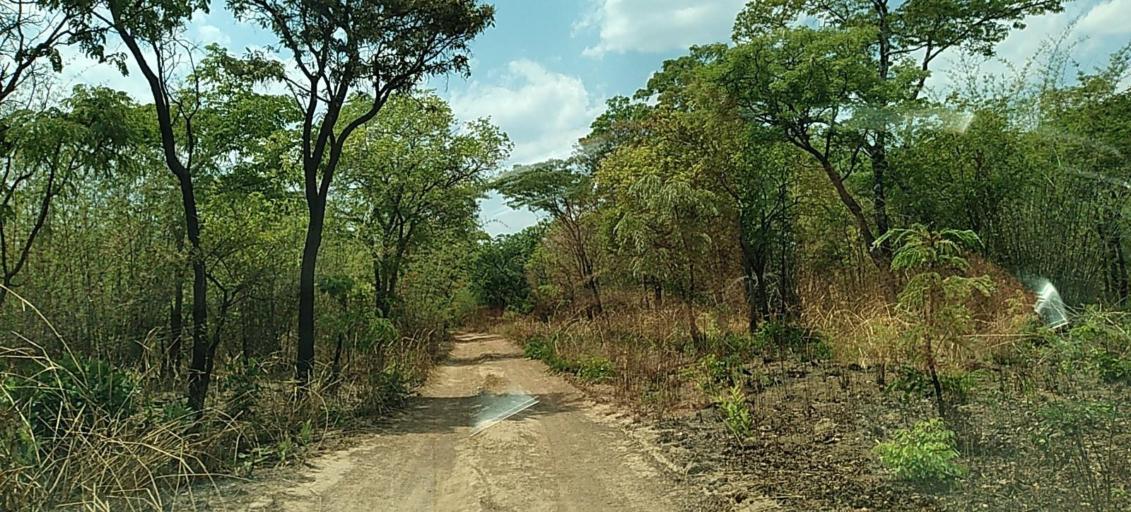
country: ZM
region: Copperbelt
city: Chililabombwe
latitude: -12.4691
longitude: 27.6499
